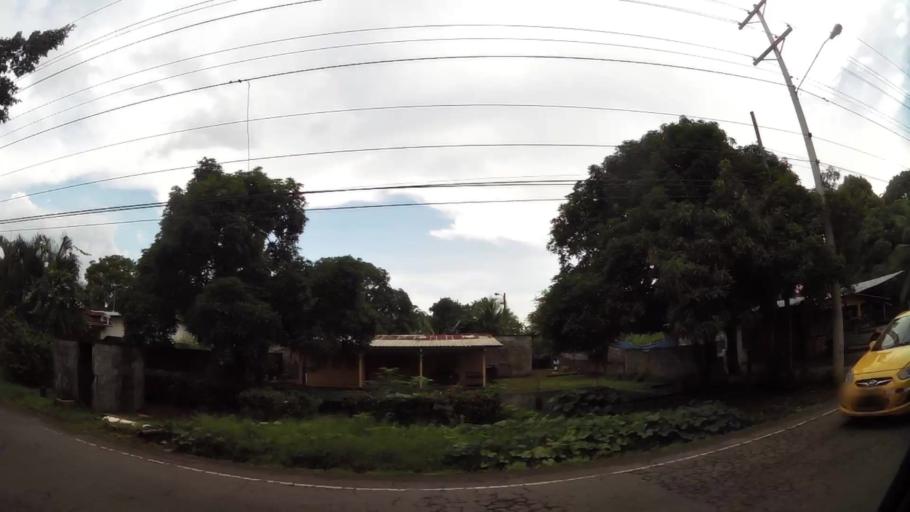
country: PA
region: Panama
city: Cabra Numero Uno
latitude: 9.1126
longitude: -79.3455
